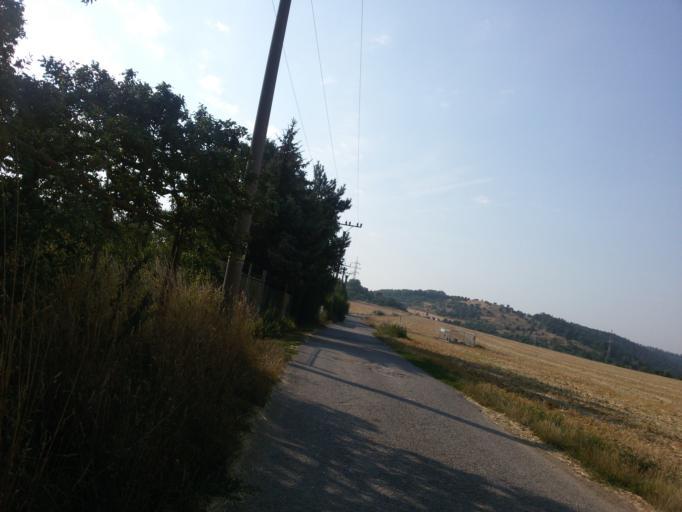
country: CZ
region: South Moravian
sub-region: Mesto Brno
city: Mokra Hora
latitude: 49.2418
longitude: 16.5639
